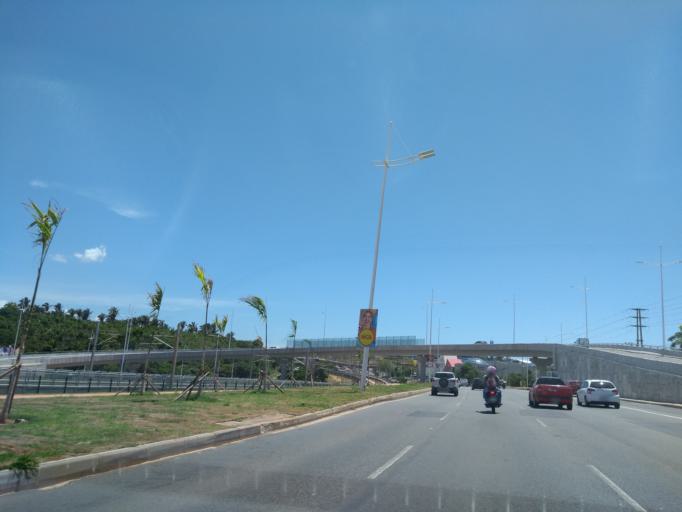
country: BR
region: Bahia
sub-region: Lauro De Freitas
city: Lauro de Freitas
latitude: -12.9373
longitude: -38.3996
